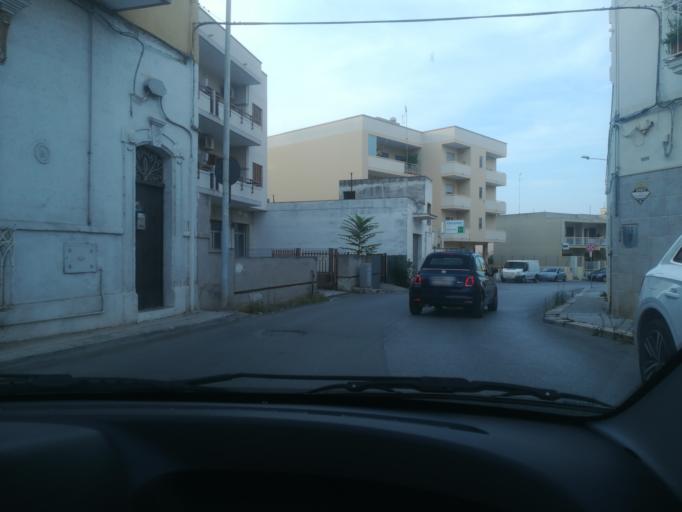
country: IT
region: Apulia
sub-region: Provincia di Bari
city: Monopoli
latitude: 40.9454
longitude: 17.2997
